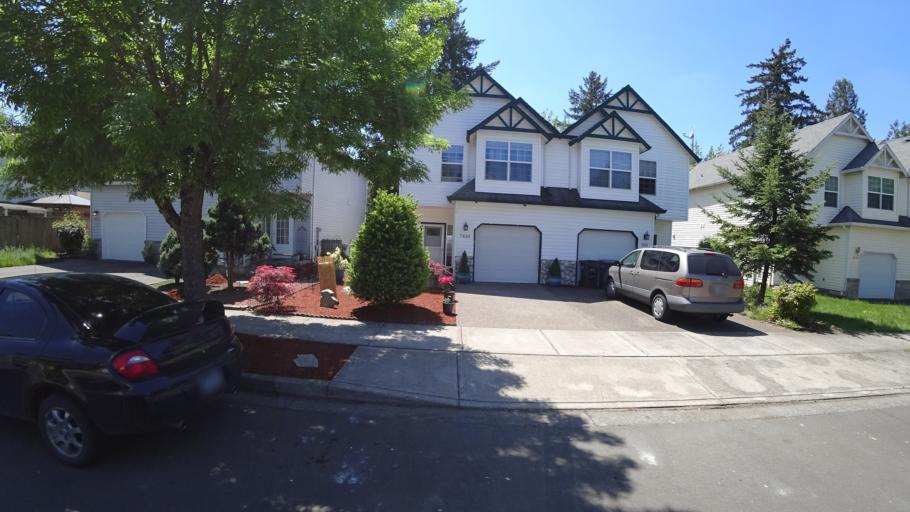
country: US
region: Oregon
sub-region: Washington County
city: Rockcreek
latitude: 45.5175
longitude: -122.9015
